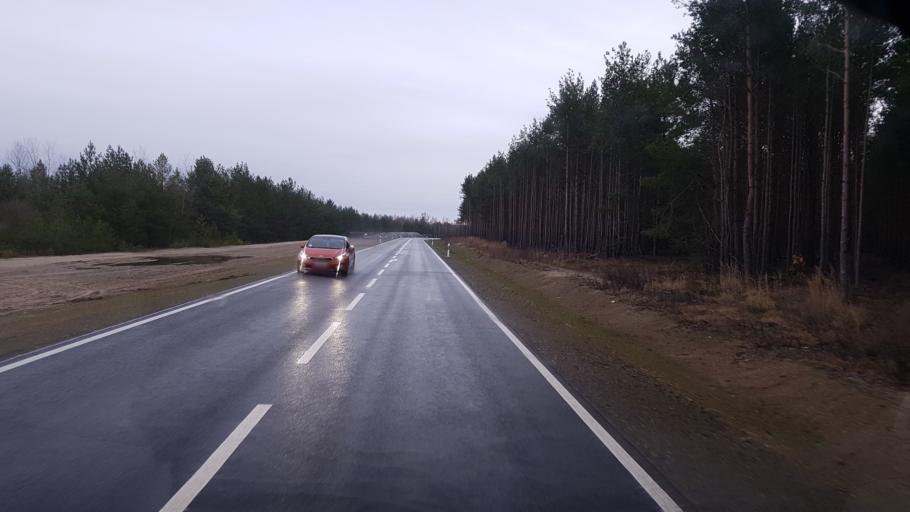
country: DE
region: Brandenburg
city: Lauchhammer
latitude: 51.5239
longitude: 13.7900
